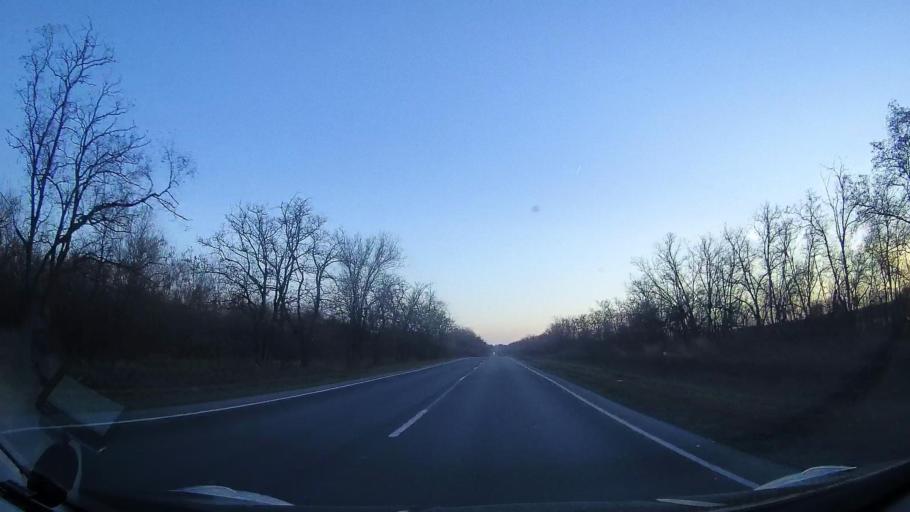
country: RU
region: Rostov
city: Bagayevskaya
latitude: 47.1248
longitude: 40.2766
